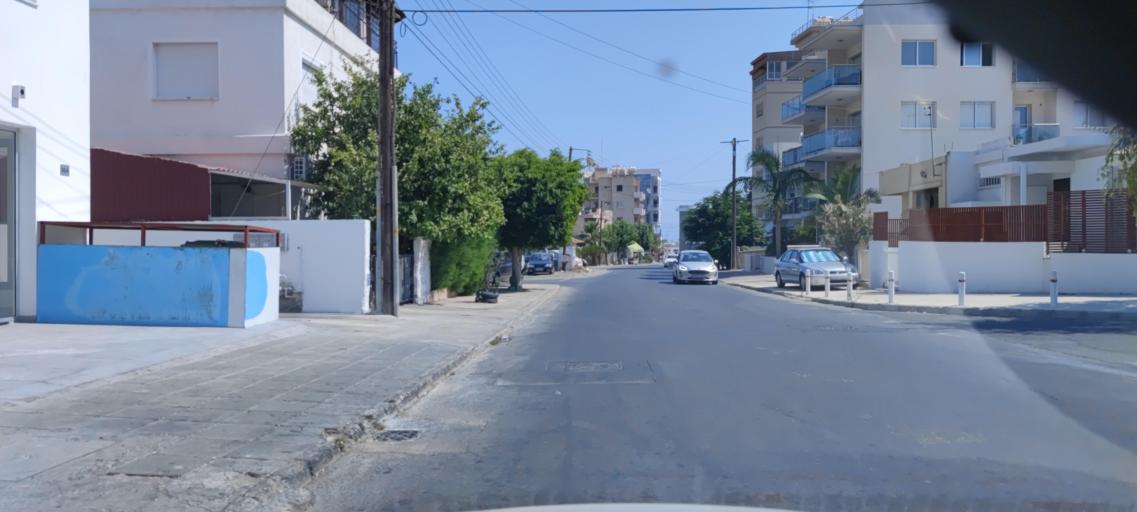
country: CY
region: Limassol
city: Limassol
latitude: 34.7009
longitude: 33.0515
